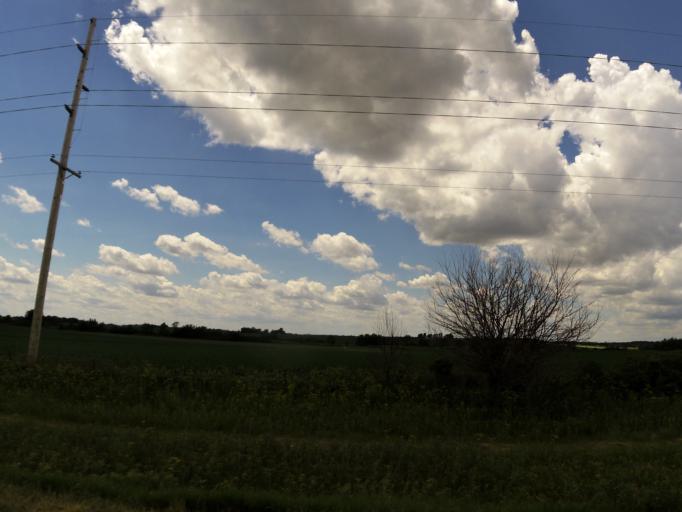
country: US
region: Iowa
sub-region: Buchanan County
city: Independence
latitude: 42.5481
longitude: -91.9049
